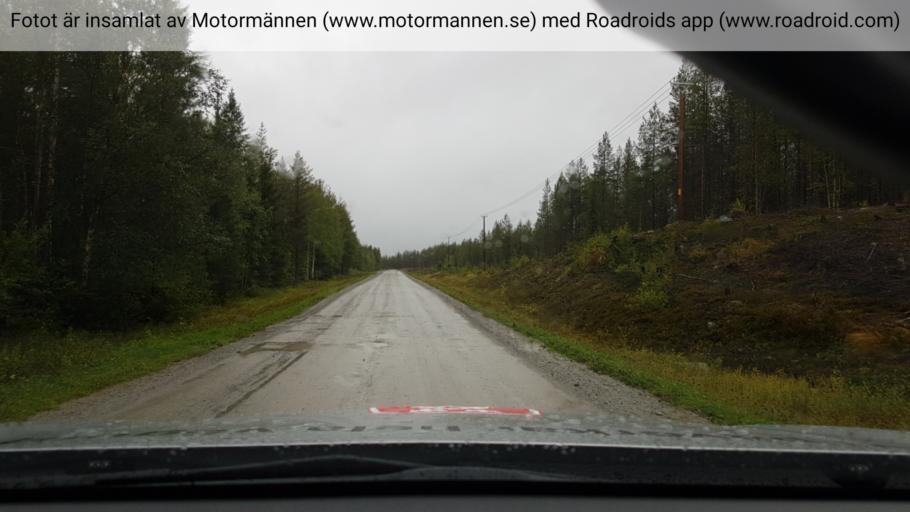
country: SE
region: Vaesterbotten
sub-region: Asele Kommun
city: Asele
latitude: 64.0640
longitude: 17.6583
